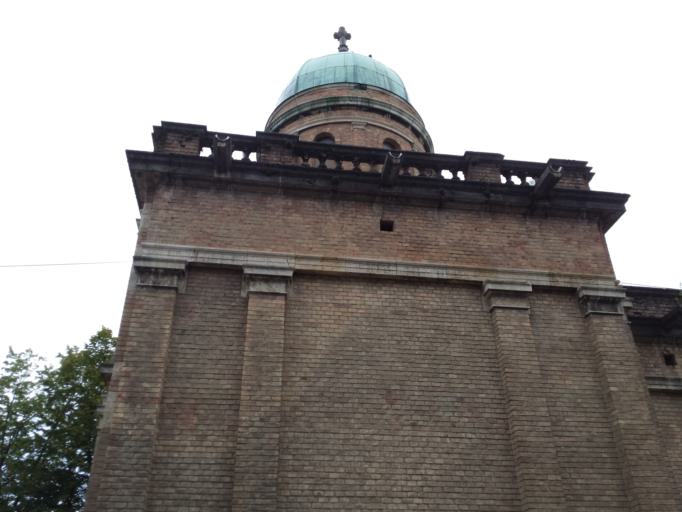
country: HR
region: Grad Zagreb
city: Zagreb
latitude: 45.8370
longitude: 15.9840
